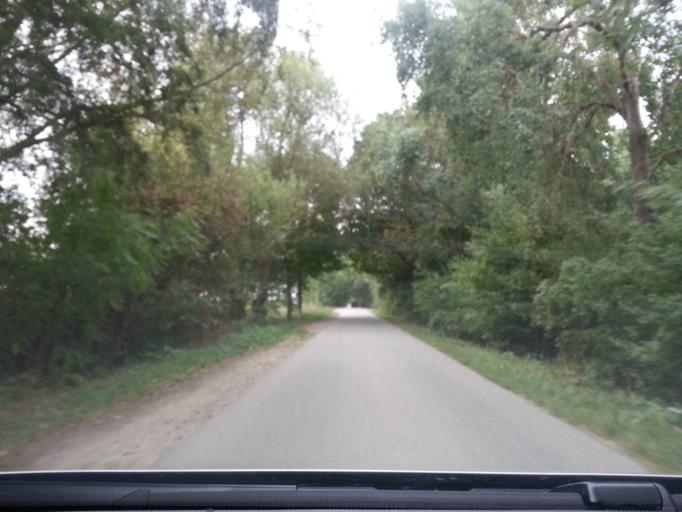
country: DE
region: Mecklenburg-Vorpommern
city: Ferdinandshof
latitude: 53.6720
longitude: 13.9159
